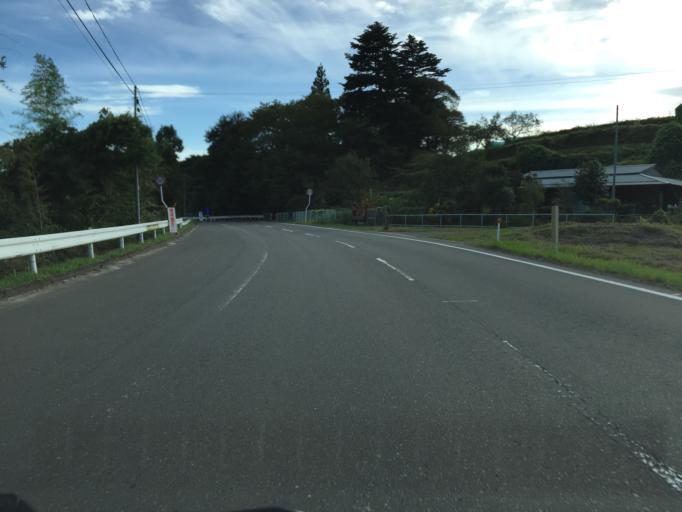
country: JP
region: Fukushima
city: Yanagawamachi-saiwaicho
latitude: 37.8293
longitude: 140.6129
